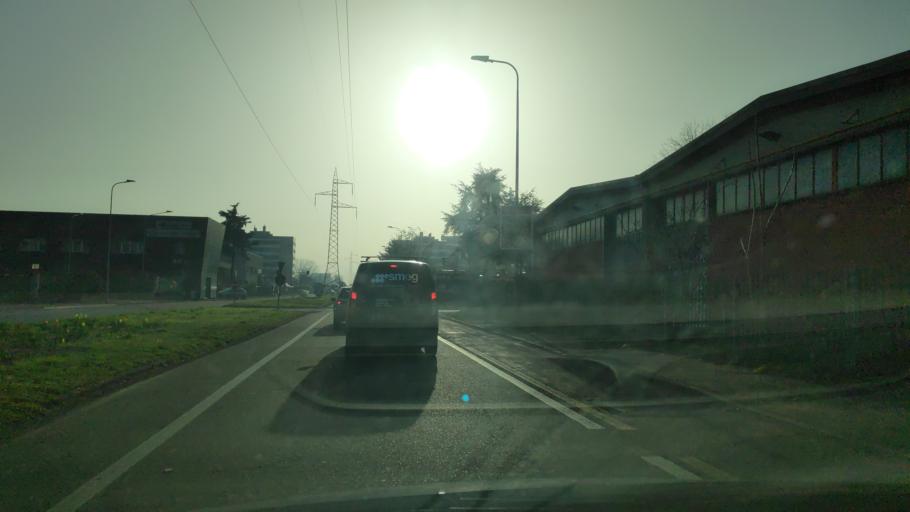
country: IT
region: Lombardy
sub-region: Citta metropolitana di Milano
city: Rozzano
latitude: 45.3943
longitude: 9.1551
